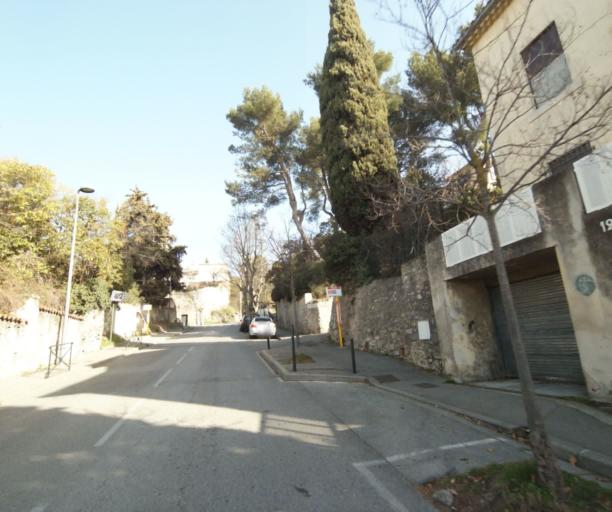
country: FR
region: Provence-Alpes-Cote d'Azur
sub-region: Departement des Bouches-du-Rhone
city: Aix-en-Provence
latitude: 43.5344
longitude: 5.4512
